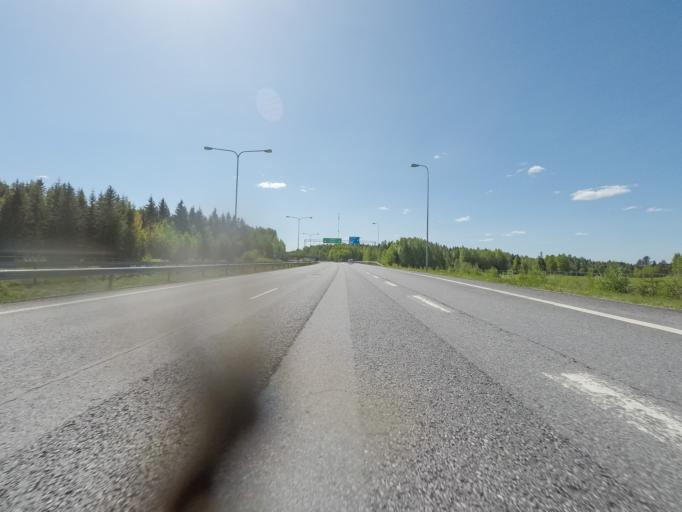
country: FI
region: Pirkanmaa
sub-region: Etelae-Pirkanmaa
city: Toijala
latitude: 61.1999
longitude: 23.8244
